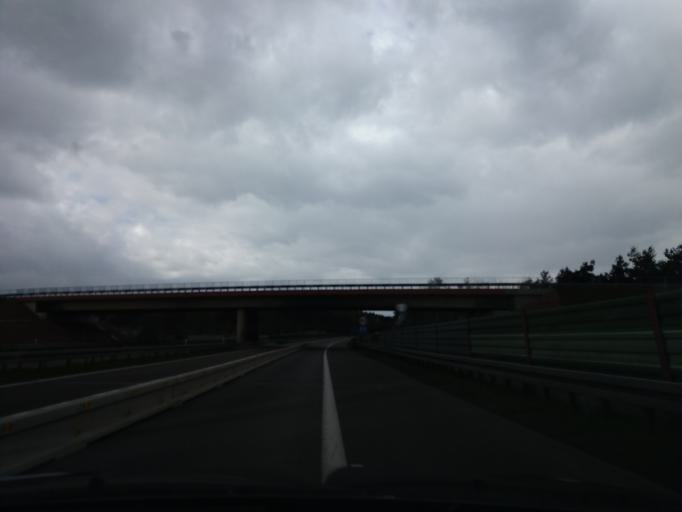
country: PL
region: Opole Voivodeship
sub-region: Powiat krapkowicki
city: Krapkowice
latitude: 50.4893
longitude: 17.9866
